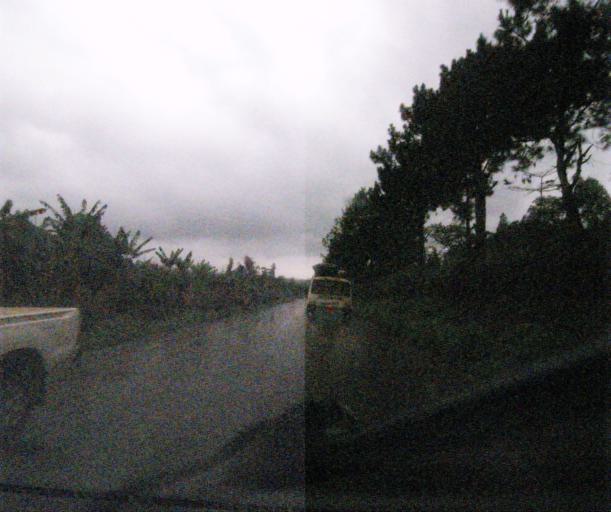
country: CM
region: West
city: Bansoa
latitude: 5.4839
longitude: 10.2715
